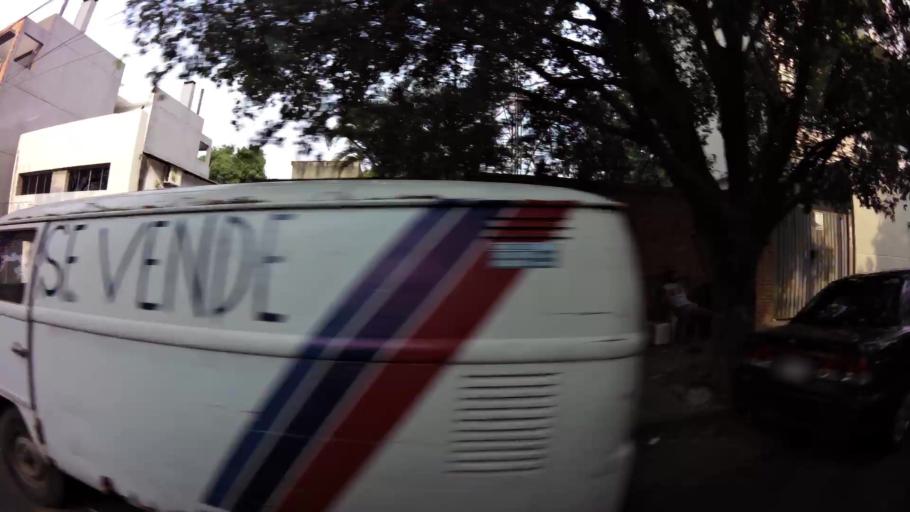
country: PY
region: Asuncion
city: Asuncion
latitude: -25.2971
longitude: -57.6095
